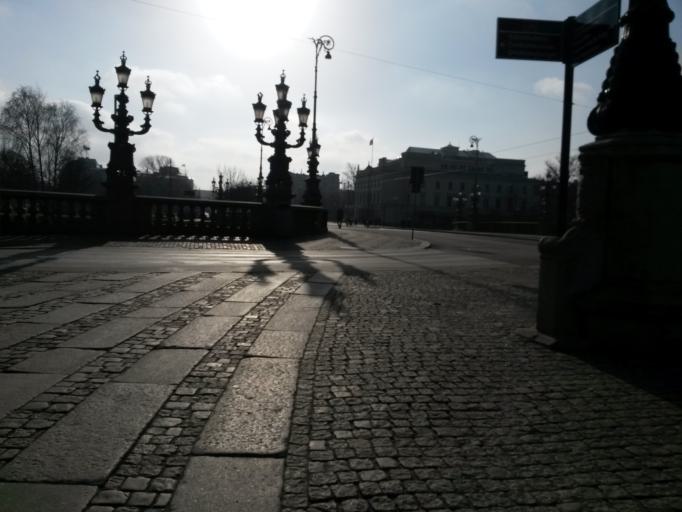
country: SE
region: Vaestra Goetaland
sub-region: Goteborg
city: Goeteborg
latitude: 57.7040
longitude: 11.9702
